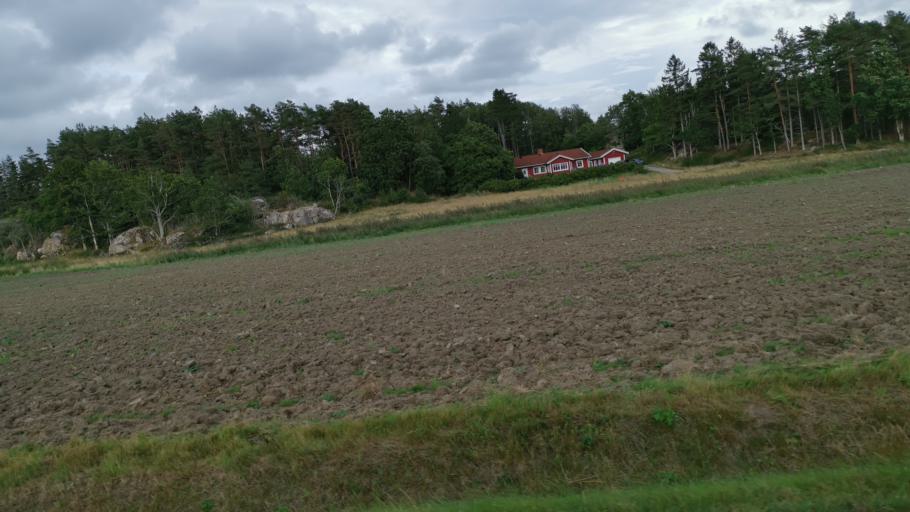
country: SE
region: Vaestra Goetaland
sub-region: Sotenas Kommun
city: Hunnebostrand
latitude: 58.5274
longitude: 11.2959
